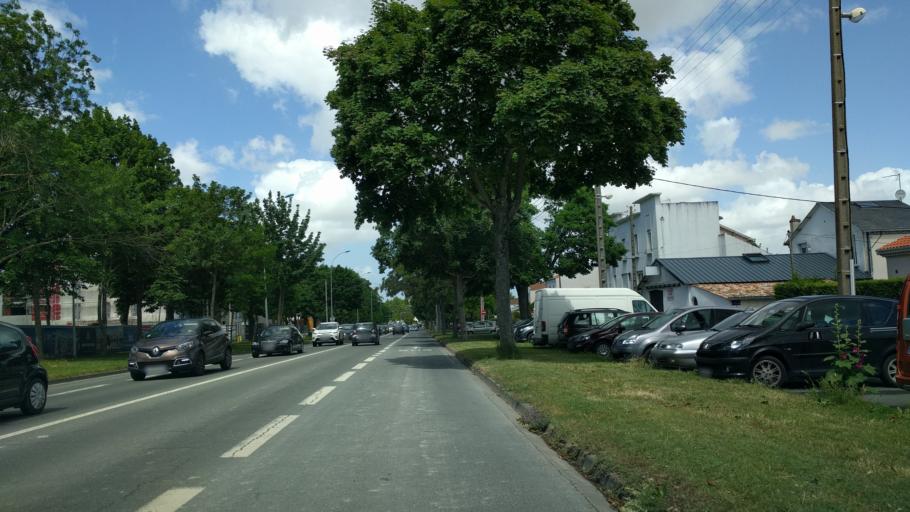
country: FR
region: Poitou-Charentes
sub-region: Departement de la Charente-Maritime
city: La Rochelle
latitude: 46.1683
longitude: -1.1430
